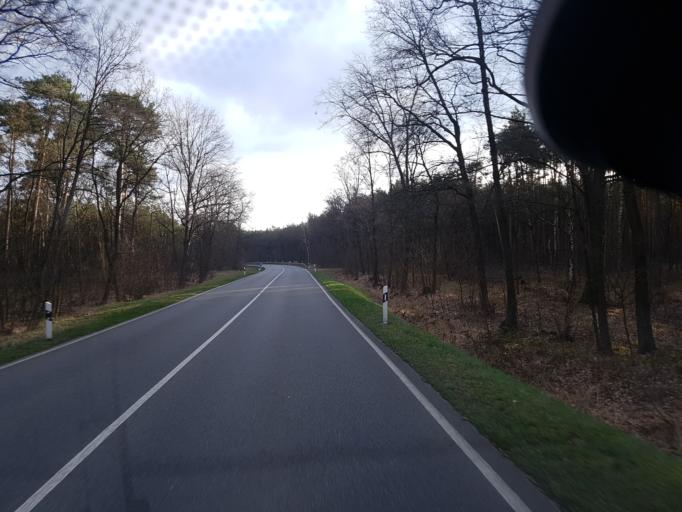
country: DE
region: Brandenburg
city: Luebben
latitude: 51.9617
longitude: 13.9415
